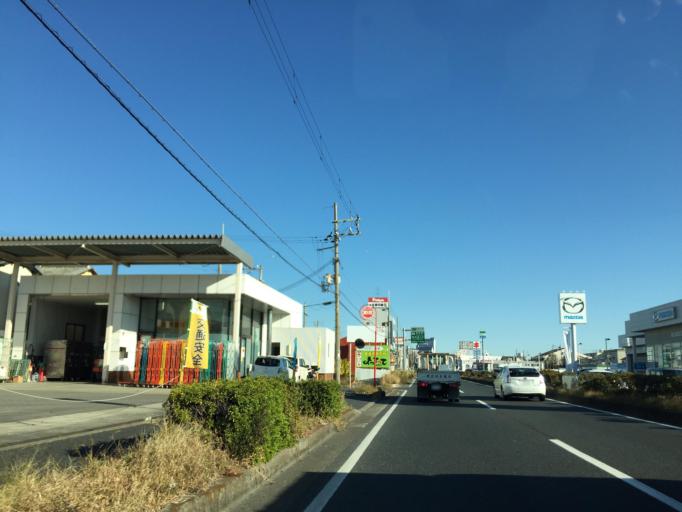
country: JP
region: Osaka
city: Kaizuka
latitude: 34.3955
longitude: 135.3074
